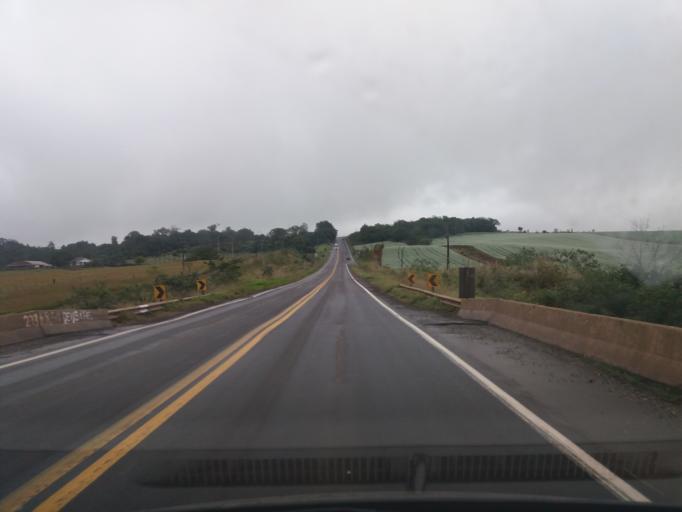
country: BR
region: Parana
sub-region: Realeza
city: Realeza
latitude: -25.5615
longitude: -53.5804
